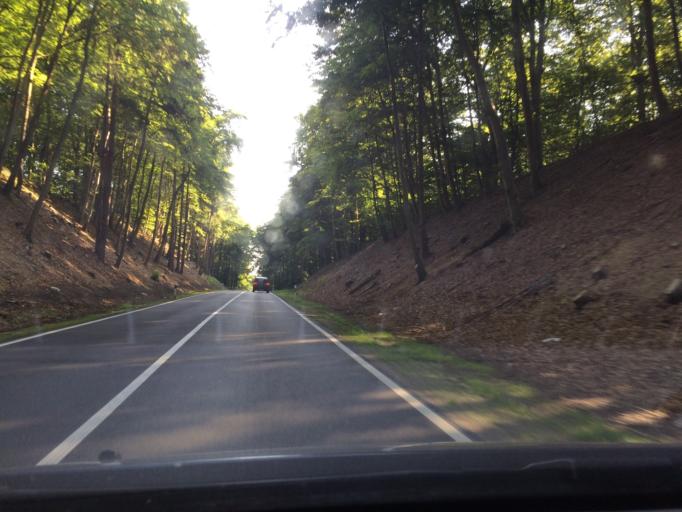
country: DE
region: Mecklenburg-Vorpommern
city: Ostseebad Binz
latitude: 54.4329
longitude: 13.5542
